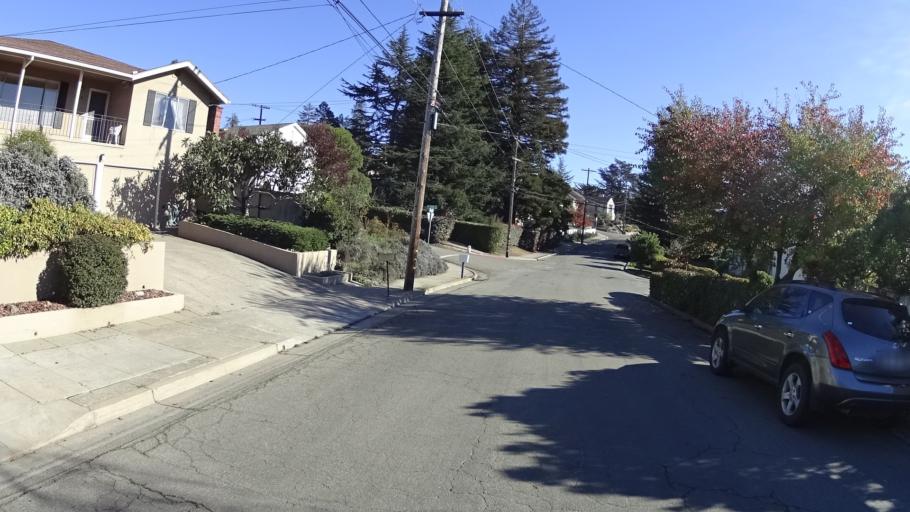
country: US
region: California
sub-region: Alameda County
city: Piedmont
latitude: 37.8351
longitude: -122.2244
